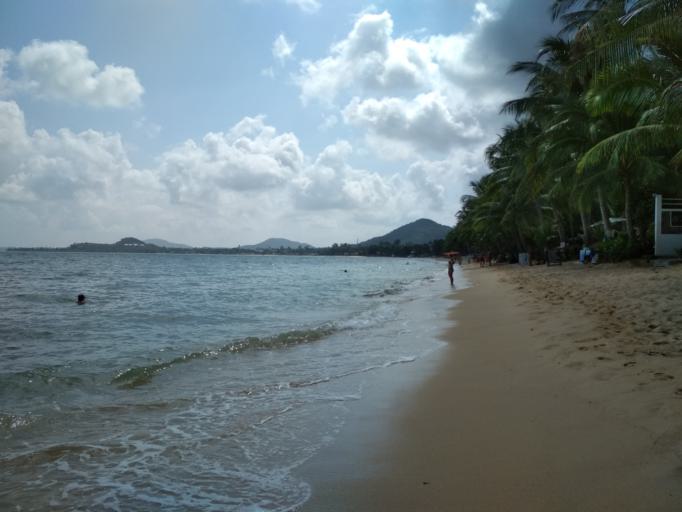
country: TH
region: Surat Thani
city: Ko Samui
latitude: 9.5755
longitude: 99.9917
